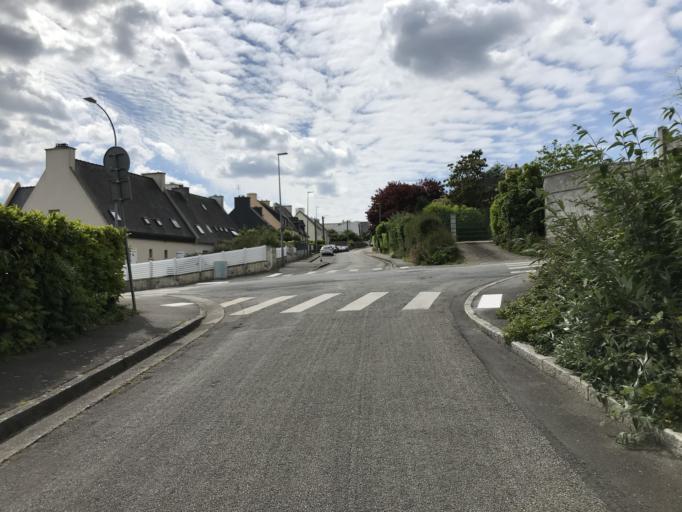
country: FR
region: Brittany
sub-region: Departement du Finistere
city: Brest
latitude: 48.3965
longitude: -4.4441
